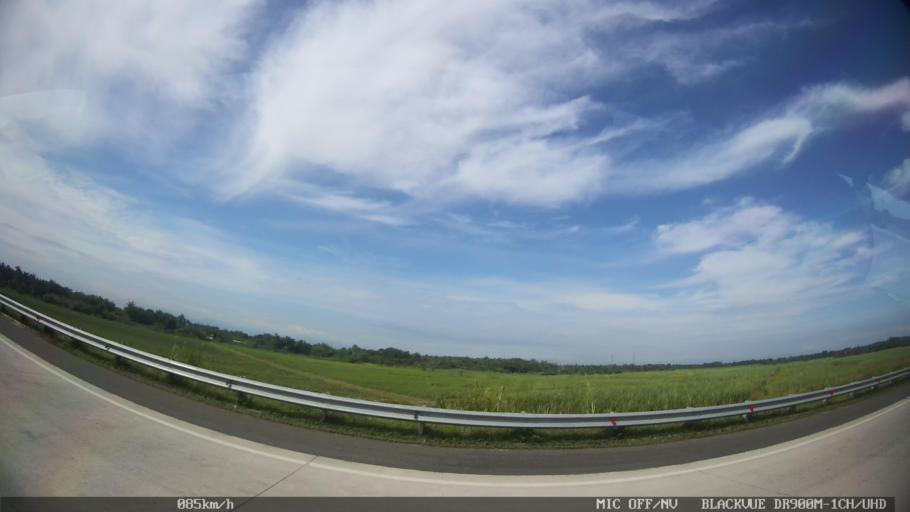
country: ID
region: North Sumatra
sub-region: Kabupaten Langkat
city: Stabat
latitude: 3.7071
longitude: 98.5362
